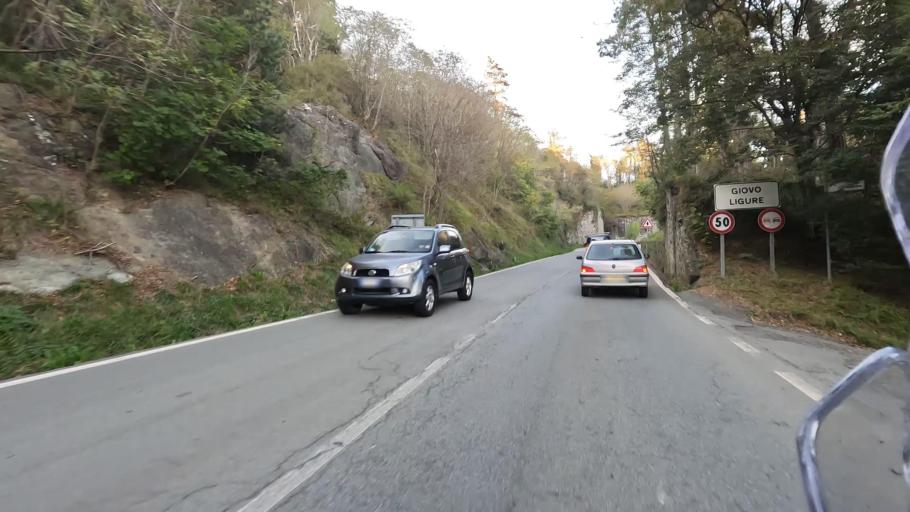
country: IT
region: Liguria
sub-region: Provincia di Savona
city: Osteria dei Cacciatori-Stella
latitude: 44.4274
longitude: 8.4731
